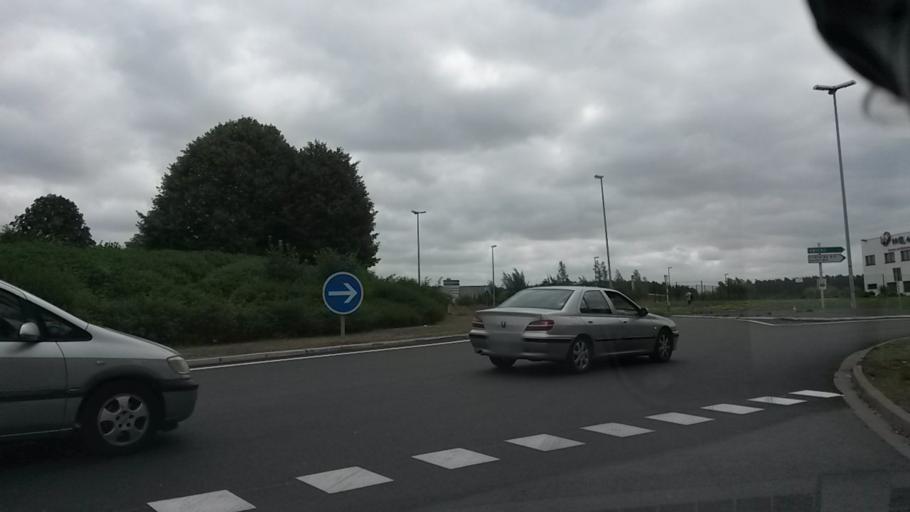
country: FR
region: Nord-Pas-de-Calais
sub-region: Departement du Nord
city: Proville
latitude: 50.1750
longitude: 3.1969
